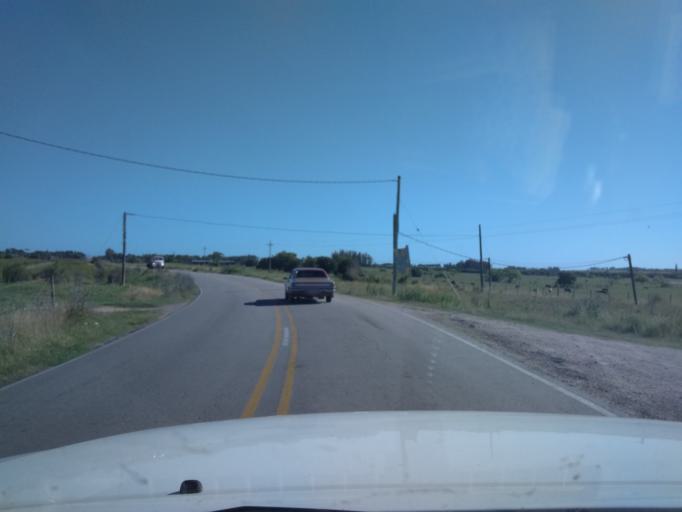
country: UY
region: Canelones
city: San Ramon
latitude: -34.3198
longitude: -55.9598
